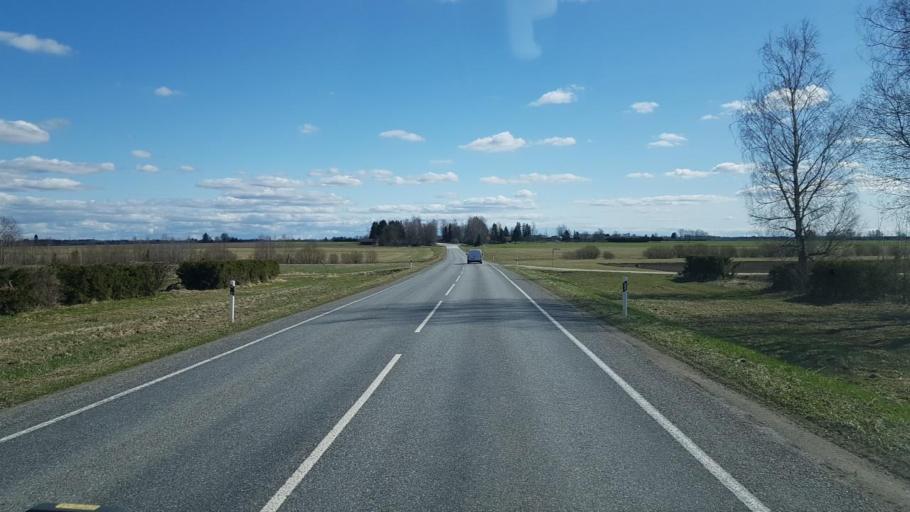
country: EE
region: Jogevamaa
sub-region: Jogeva linn
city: Jogeva
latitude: 58.8039
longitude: 26.5137
